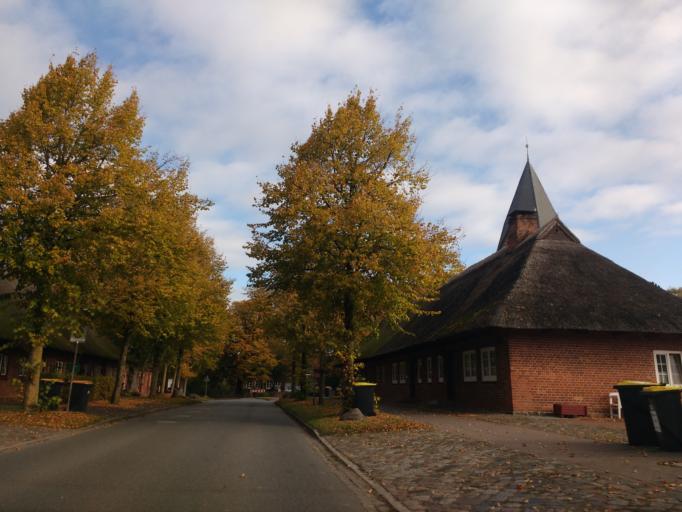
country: DE
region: Schleswig-Holstein
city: Altenkrempe
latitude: 54.1325
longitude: 10.8251
